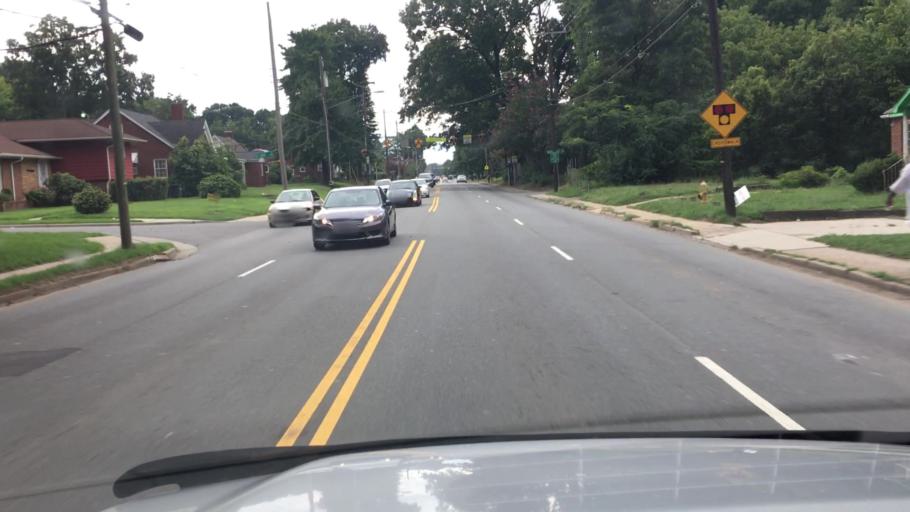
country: US
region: North Carolina
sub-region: Mecklenburg County
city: Charlotte
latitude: 35.2610
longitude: -80.8551
